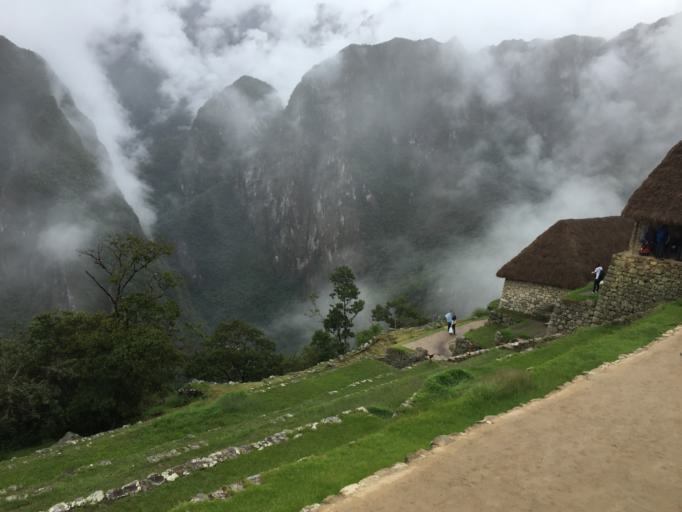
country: PE
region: Cusco
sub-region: Provincia de La Convencion
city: Santa Teresa
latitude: -13.1646
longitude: -72.5438
